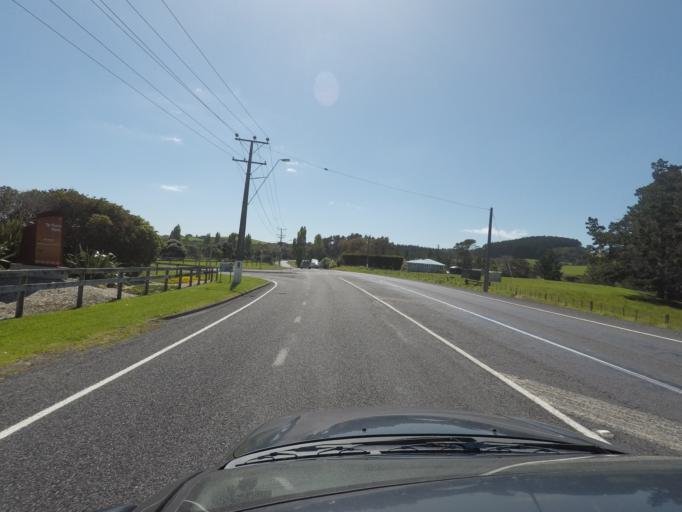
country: NZ
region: Auckland
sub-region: Auckland
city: Pakuranga
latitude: -36.8845
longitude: 175.0187
